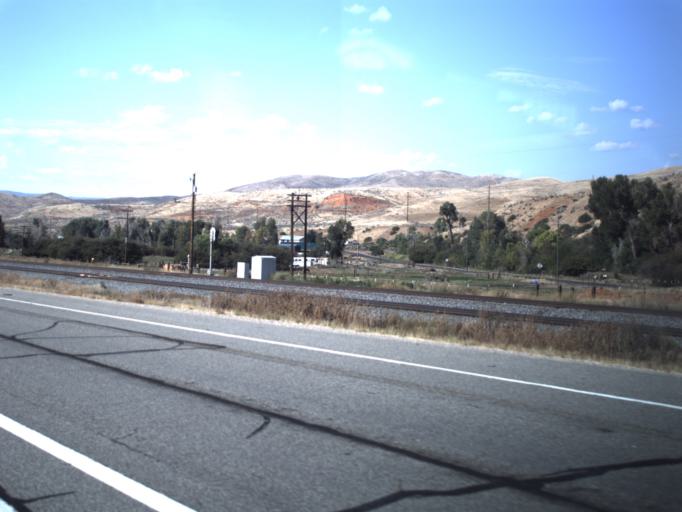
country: US
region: Utah
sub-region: Summit County
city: Coalville
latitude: 41.0202
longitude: -111.4927
